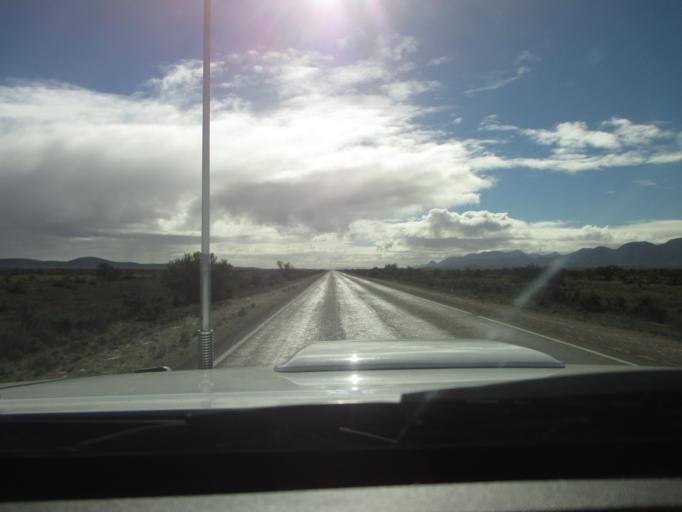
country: AU
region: South Australia
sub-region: Flinders Ranges
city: Quorn
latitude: -31.6954
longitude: 138.3593
